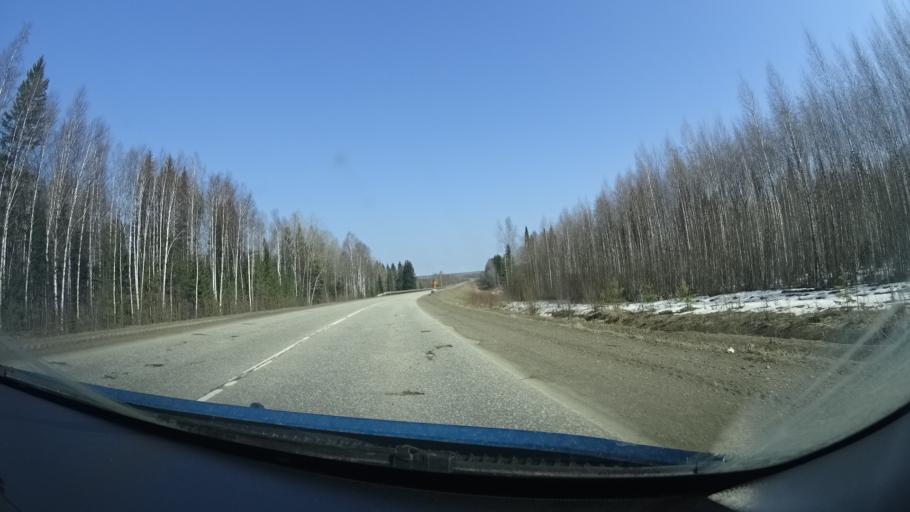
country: RU
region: Perm
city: Osa
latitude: 57.4383
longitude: 55.6286
